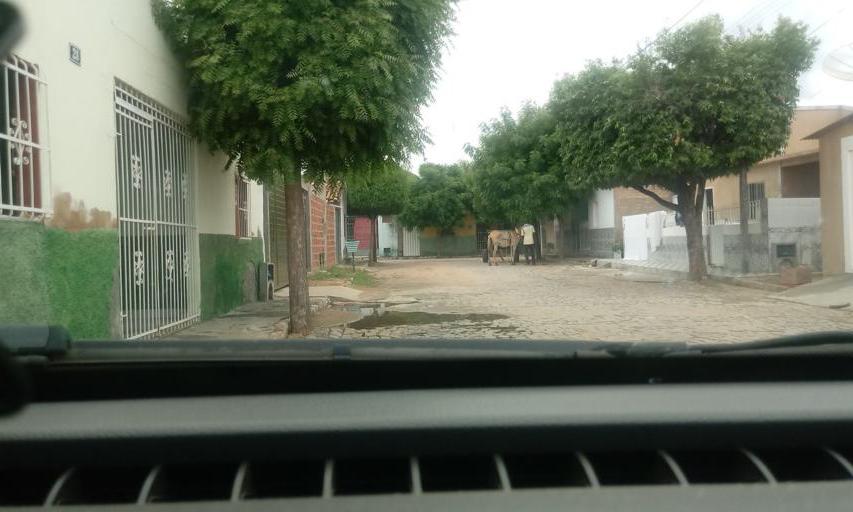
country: BR
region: Bahia
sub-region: Riacho De Santana
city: Riacho de Santana
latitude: -13.9125
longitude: -42.8457
